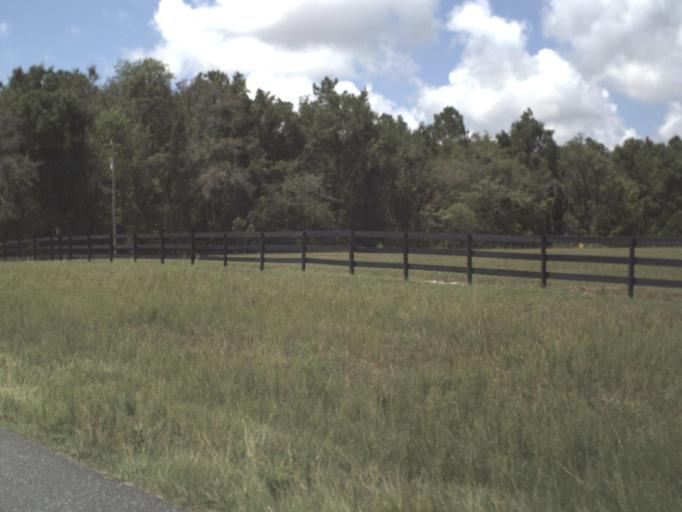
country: US
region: Florida
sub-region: Gilchrist County
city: Trenton
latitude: 29.8258
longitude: -82.8673
